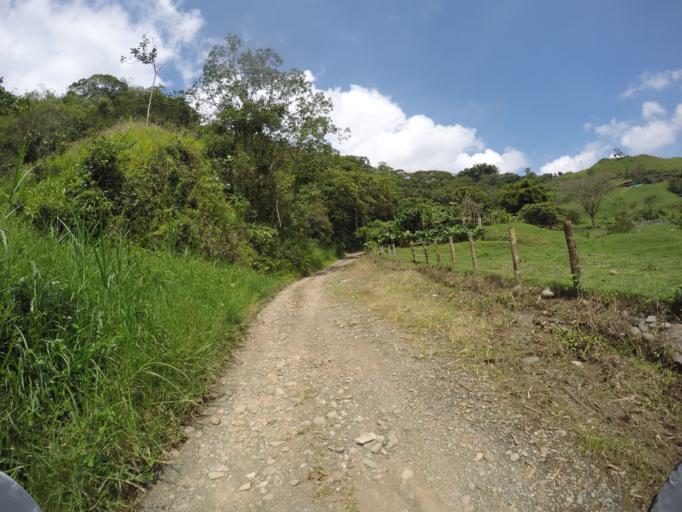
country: CO
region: Valle del Cauca
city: Ulloa
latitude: 4.6989
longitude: -75.7200
